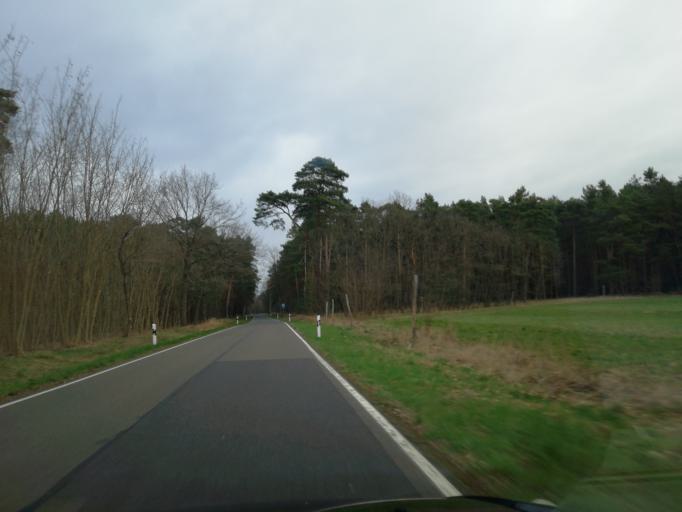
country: DE
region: Brandenburg
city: Vetschau
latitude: 51.7391
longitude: 14.1306
